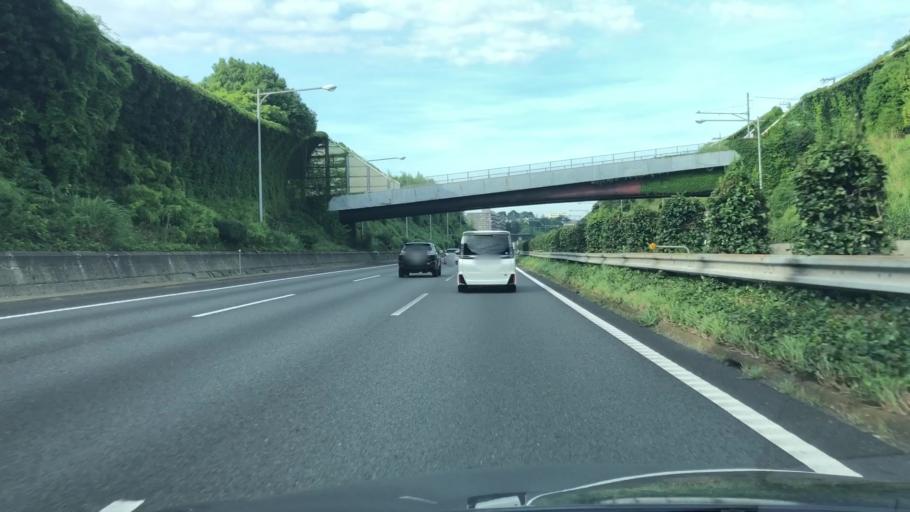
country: JP
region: Kanagawa
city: Hadano
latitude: 35.3709
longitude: 139.2629
